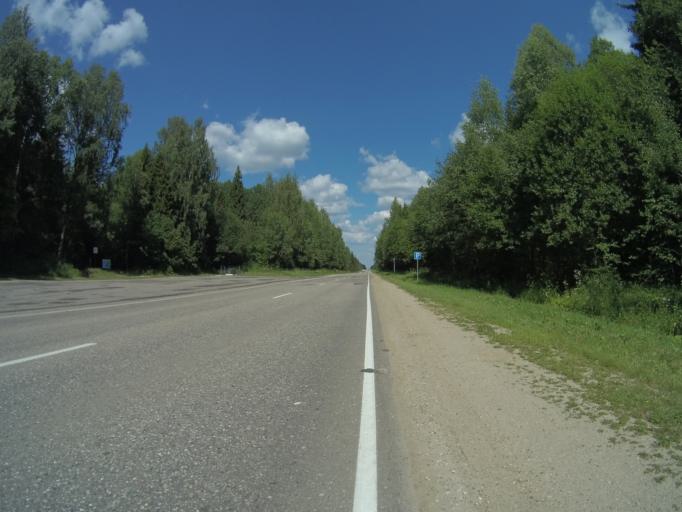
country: RU
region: Ivanovo
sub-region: Privolzhskiy Rayon
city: Ples
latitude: 57.4209
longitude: 41.4451
